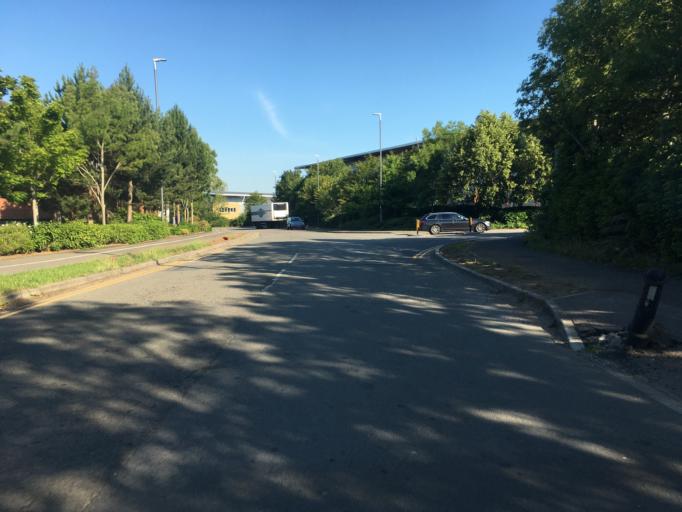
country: GB
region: England
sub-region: South Gloucestershire
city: Mangotsfield
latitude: 51.5050
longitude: -2.4826
